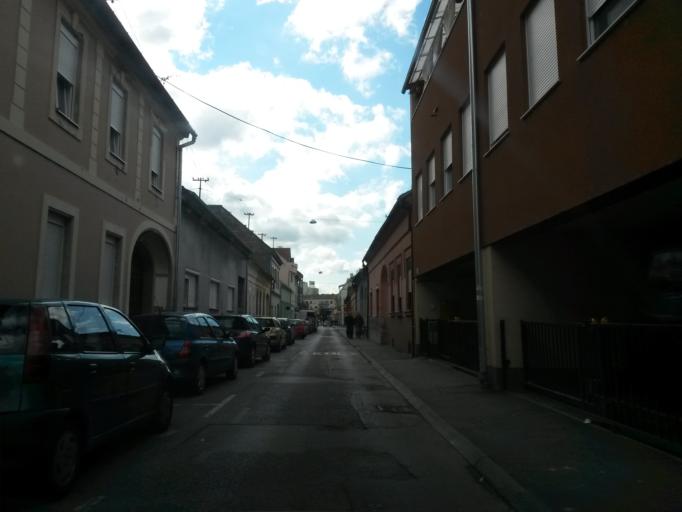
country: HR
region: Osjecko-Baranjska
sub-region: Grad Osijek
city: Osijek
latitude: 45.5582
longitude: 18.7192
